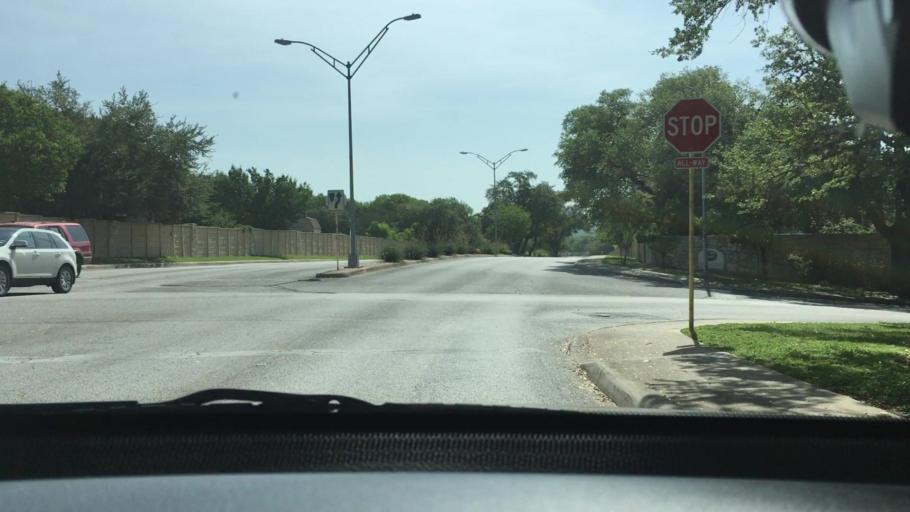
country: US
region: Texas
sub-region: Bexar County
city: Live Oak
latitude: 29.5877
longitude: -98.4052
